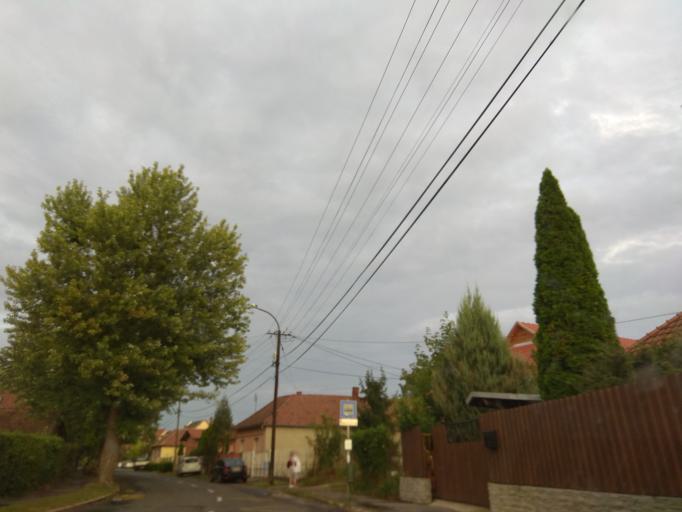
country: HU
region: Borsod-Abauj-Zemplen
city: Miskolc
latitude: 48.0558
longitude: 20.7843
